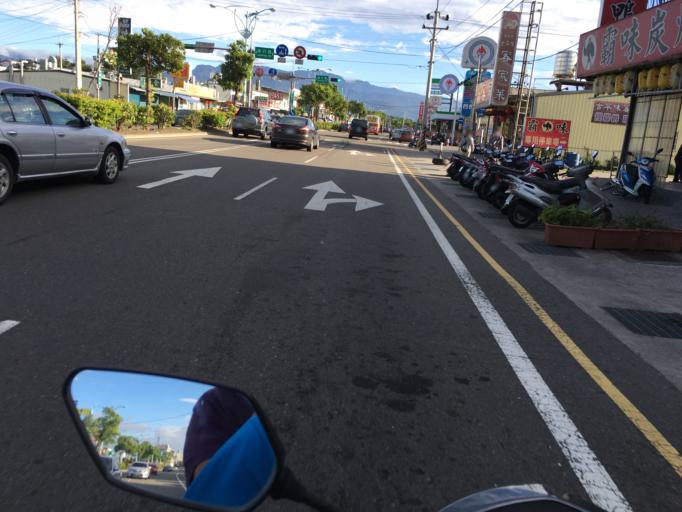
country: TW
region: Taiwan
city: Daxi
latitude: 24.8673
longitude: 121.2217
